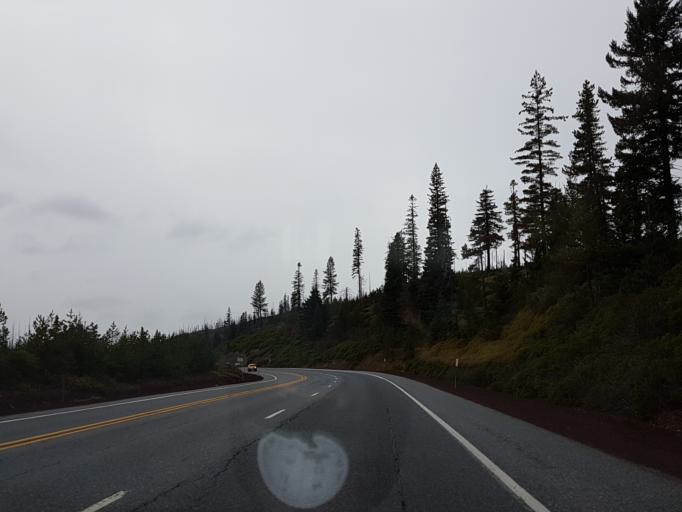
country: US
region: Oregon
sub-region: Deschutes County
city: Sisters
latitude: 44.4243
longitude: -121.8101
